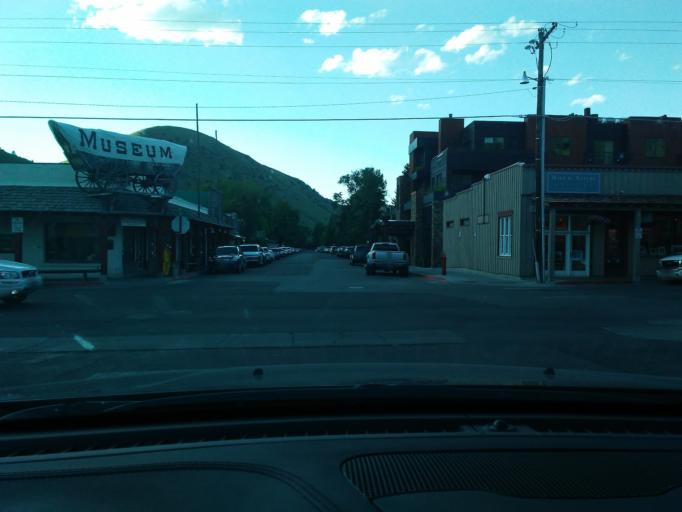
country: US
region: Wyoming
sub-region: Teton County
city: Jackson
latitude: 43.4802
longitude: -110.7638
